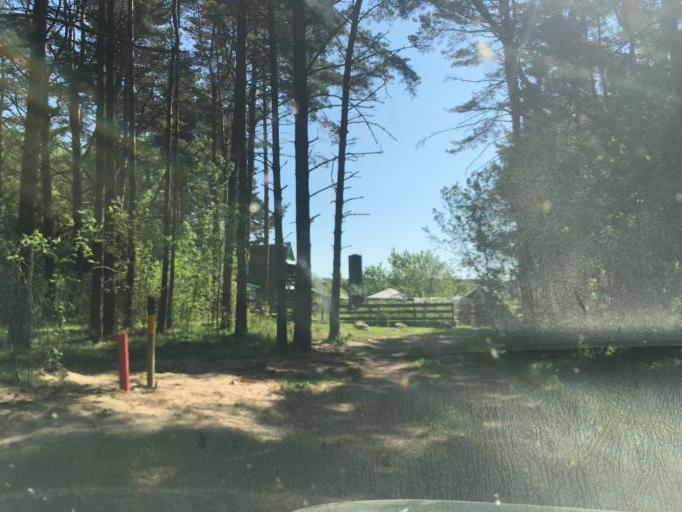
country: LV
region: Ventspils
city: Ventspils
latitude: 57.4596
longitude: 21.6446
